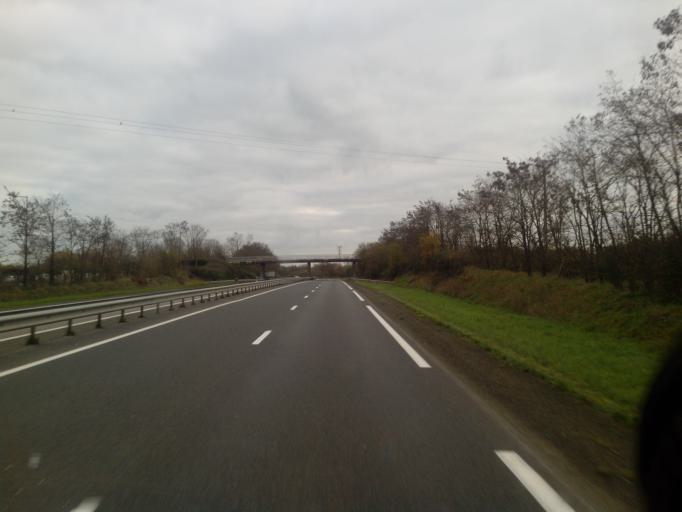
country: FR
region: Poitou-Charentes
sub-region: Departement des Deux-Sevres
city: Bressuire
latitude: 46.8442
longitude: -0.4681
